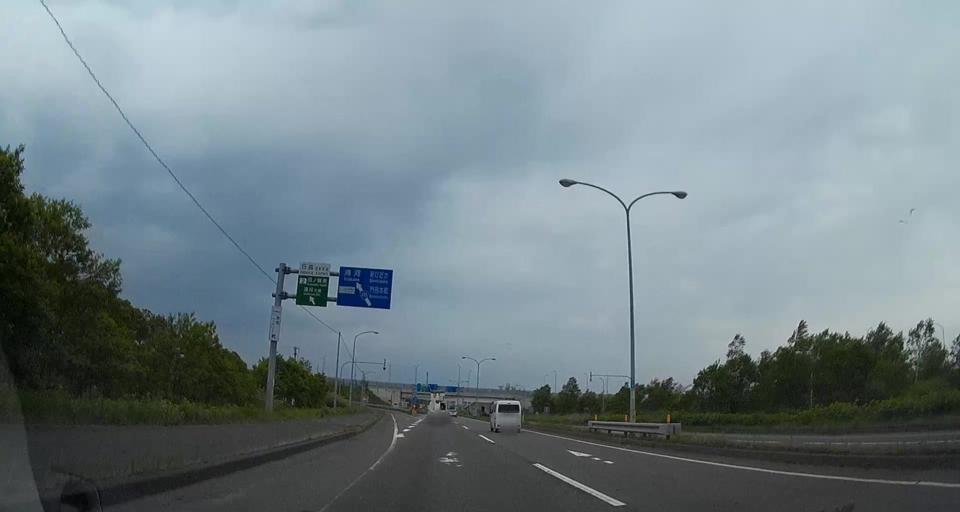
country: JP
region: Hokkaido
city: Tomakomai
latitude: 42.6789
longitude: 141.7137
